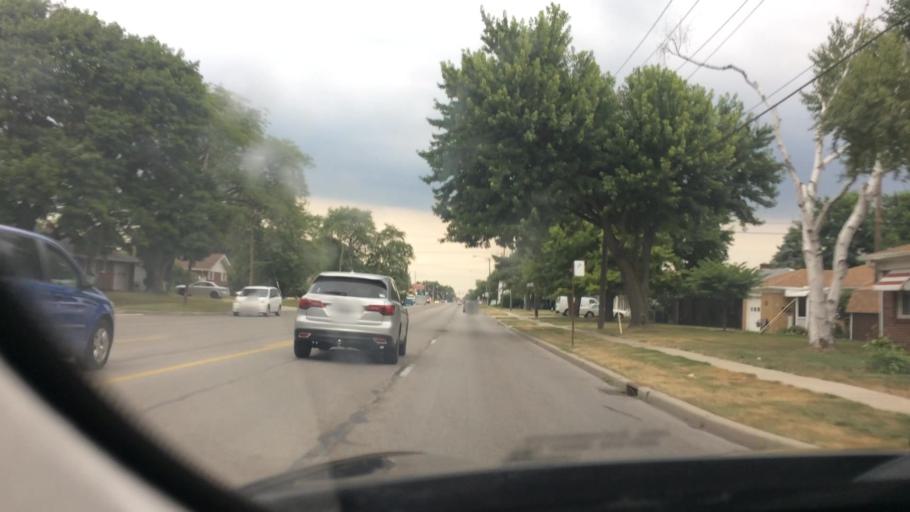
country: US
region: Ohio
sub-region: Wood County
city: Perrysburg
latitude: 41.6068
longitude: -83.6257
